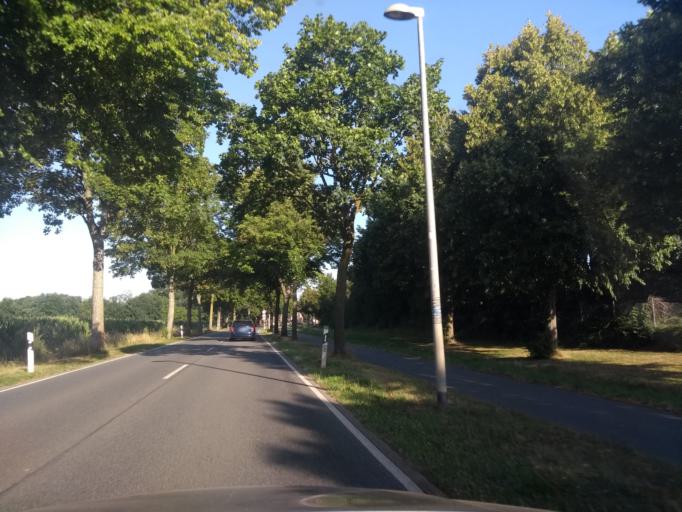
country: DE
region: North Rhine-Westphalia
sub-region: Regierungsbezirk Dusseldorf
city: Kleve
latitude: 51.8029
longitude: 6.1247
